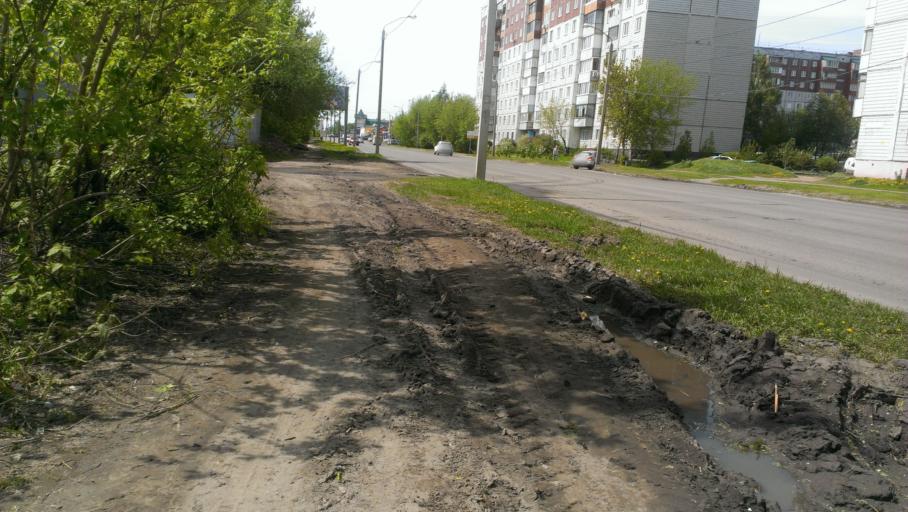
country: RU
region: Altai Krai
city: Novosilikatnyy
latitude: 53.3567
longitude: 83.6621
